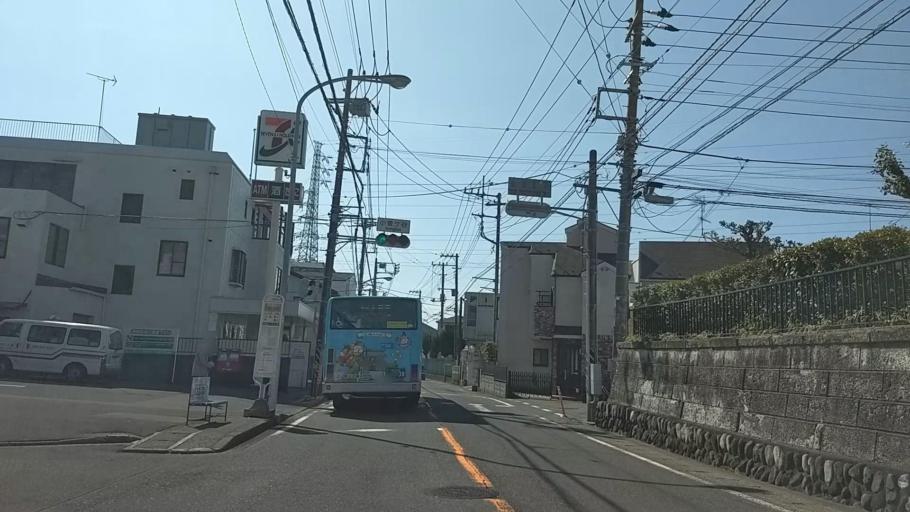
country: JP
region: Kanagawa
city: Kamakura
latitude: 35.3646
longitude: 139.5405
